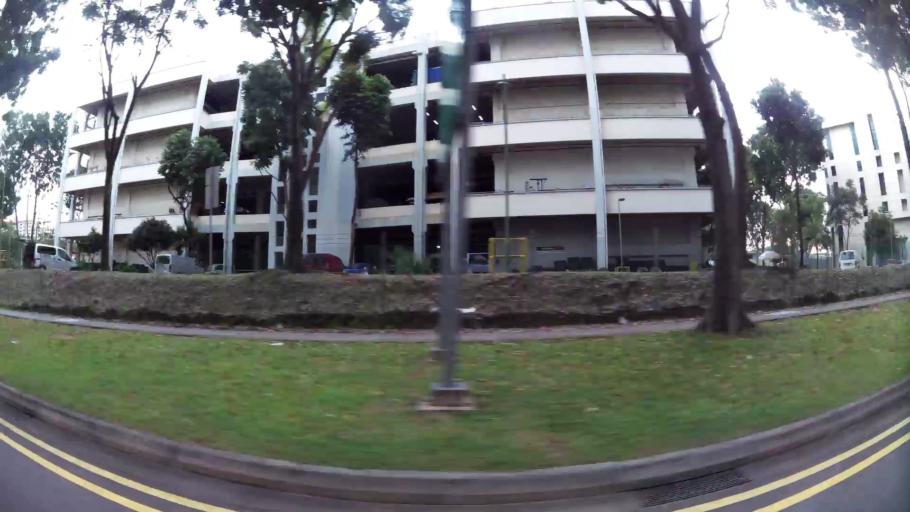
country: MY
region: Johor
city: Johor Bahru
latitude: 1.4547
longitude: 103.8116
